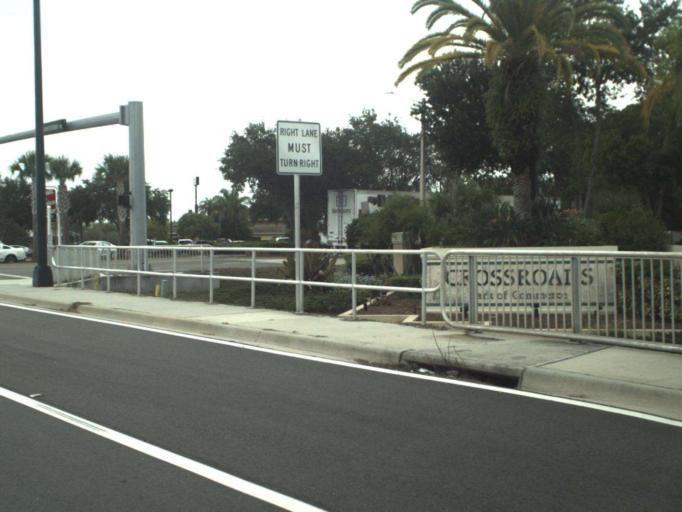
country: US
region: Florida
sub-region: Saint Lucie County
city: Fort Pierce South
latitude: 27.4138
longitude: -80.3945
